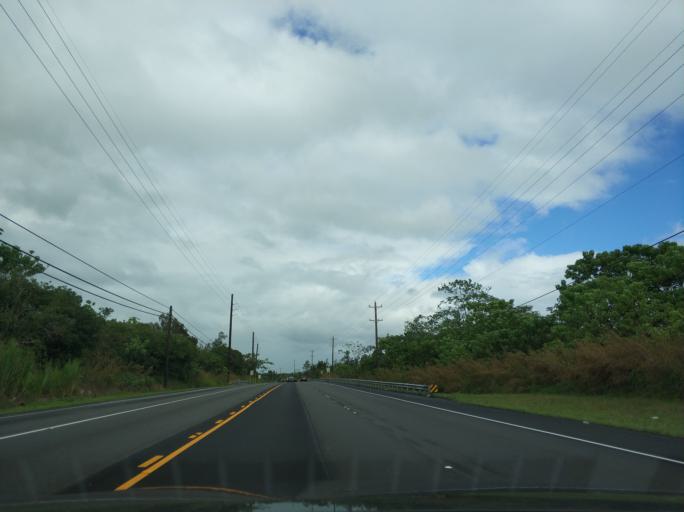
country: US
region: Hawaii
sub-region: Hawaii County
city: Orchidlands Estates
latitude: 19.5919
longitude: -155.0160
